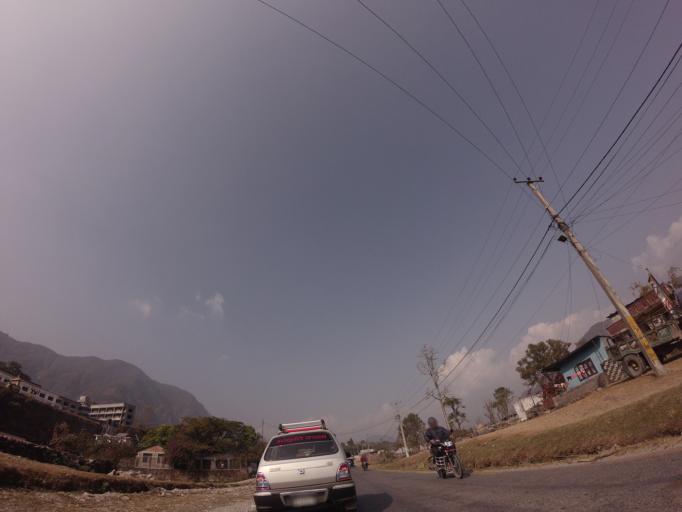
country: NP
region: Western Region
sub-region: Gandaki Zone
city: Pokhara
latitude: 28.2579
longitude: 83.9624
